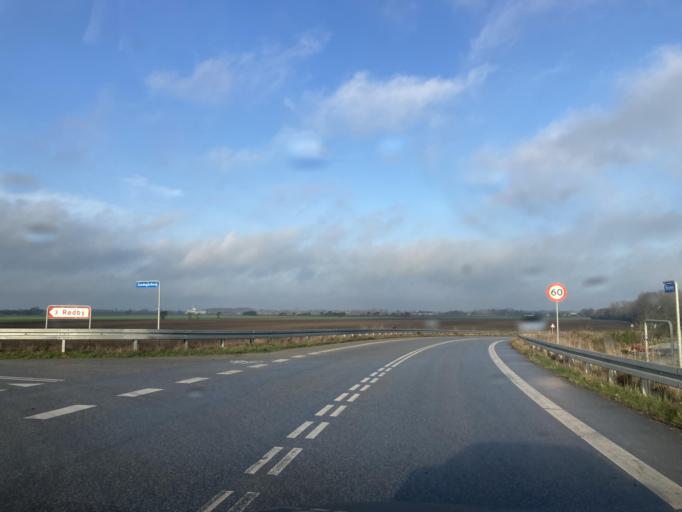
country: DK
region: Zealand
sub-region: Lolland Kommune
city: Rodby
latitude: 54.6792
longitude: 11.4247
